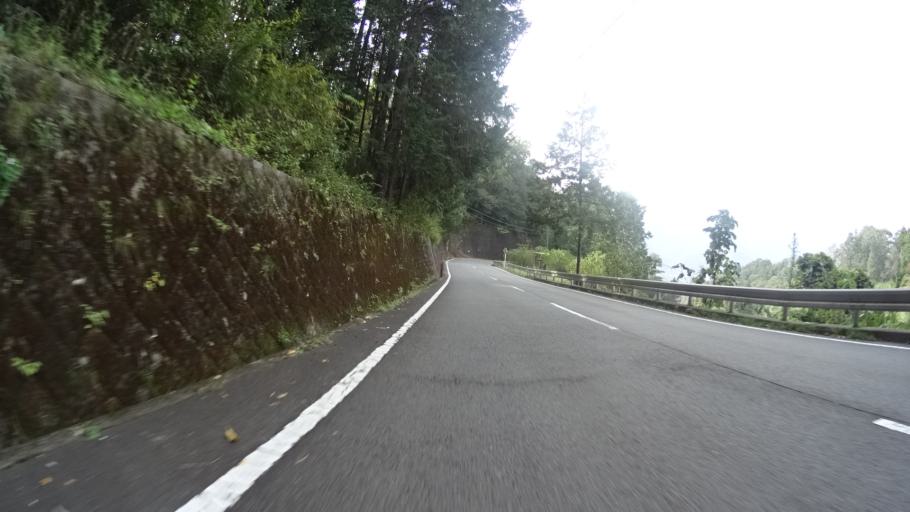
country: JP
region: Yamanashi
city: Otsuki
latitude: 35.6203
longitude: 139.0187
